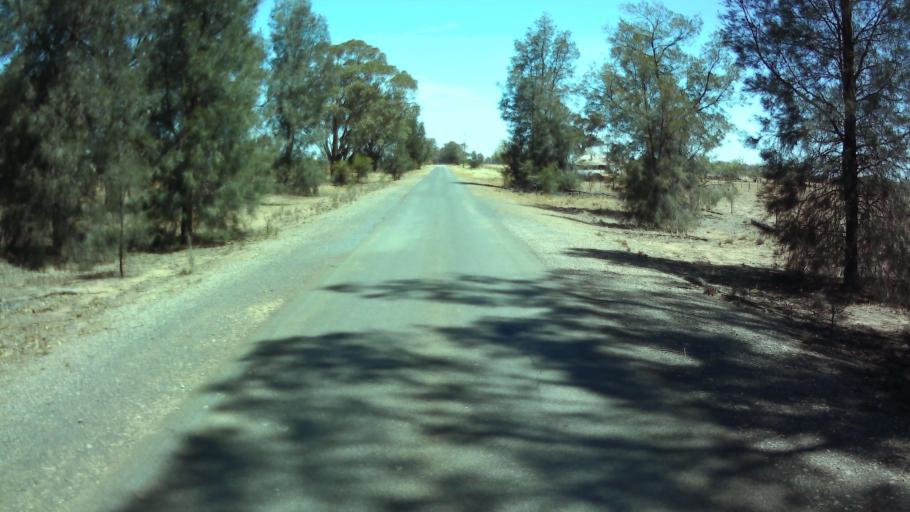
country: AU
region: New South Wales
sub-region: Weddin
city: Grenfell
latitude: -33.9038
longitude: 147.6858
